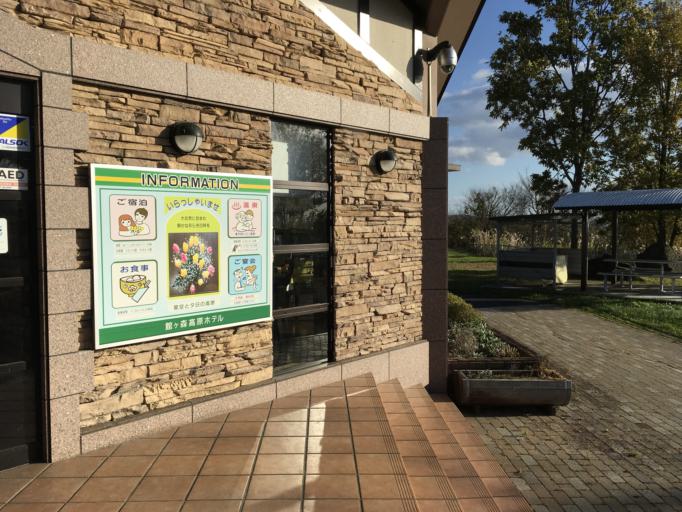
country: JP
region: Iwate
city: Ichinoseki
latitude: 38.8202
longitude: 141.2788
